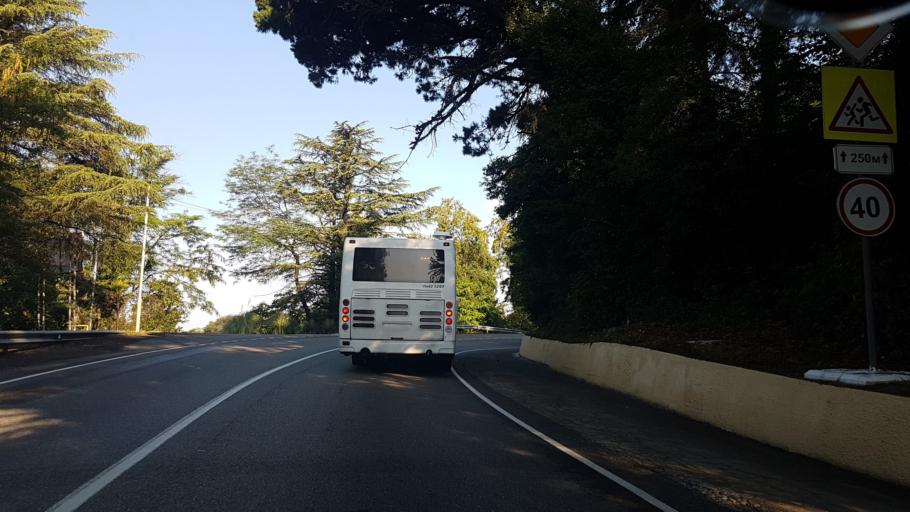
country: RU
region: Krasnodarskiy
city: Vardane
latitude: 43.7893
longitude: 39.4810
